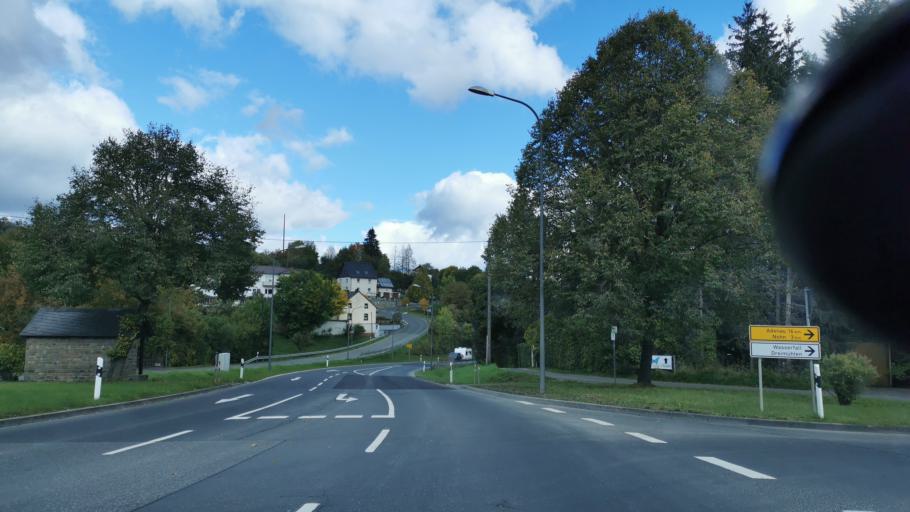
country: DE
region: Rheinland-Pfalz
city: Nohn
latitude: 50.3371
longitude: 6.7675
